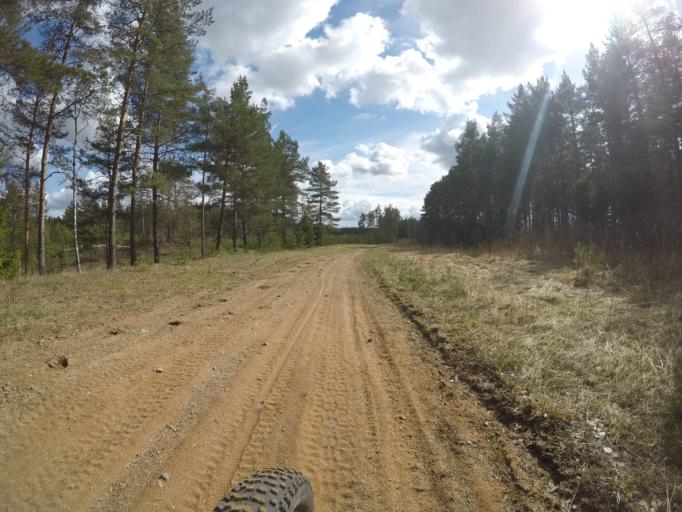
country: SE
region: Vaestmanland
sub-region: Kungsors Kommun
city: Kungsoer
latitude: 59.3489
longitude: 16.1072
